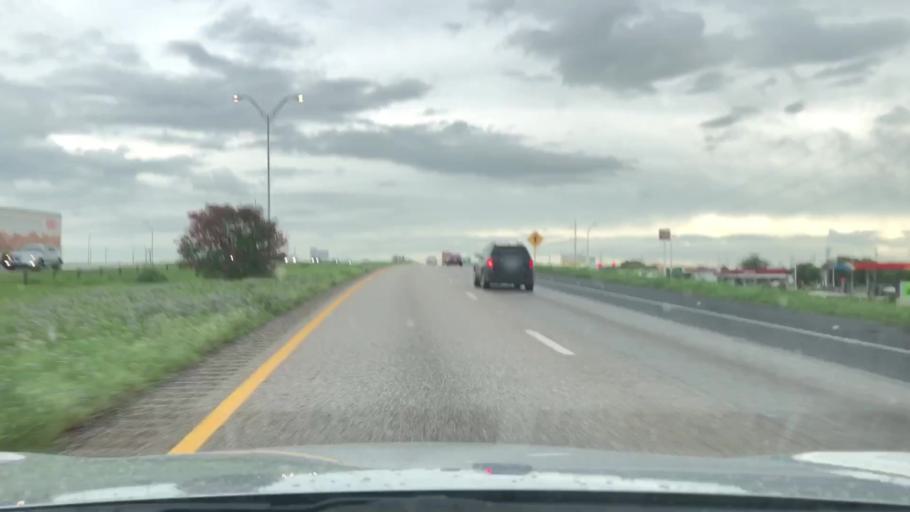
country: US
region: Texas
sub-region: Guadalupe County
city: Seguin
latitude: 29.5992
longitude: -97.9672
